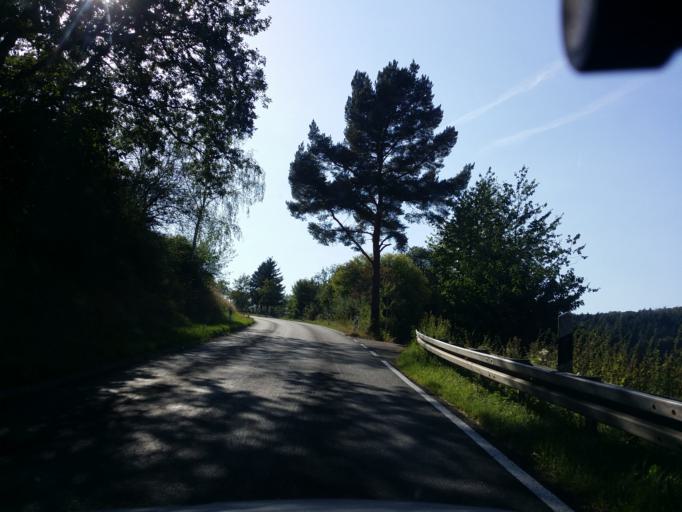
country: DE
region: Hesse
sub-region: Regierungsbezirk Darmstadt
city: Idstein
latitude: 50.1999
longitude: 8.2177
